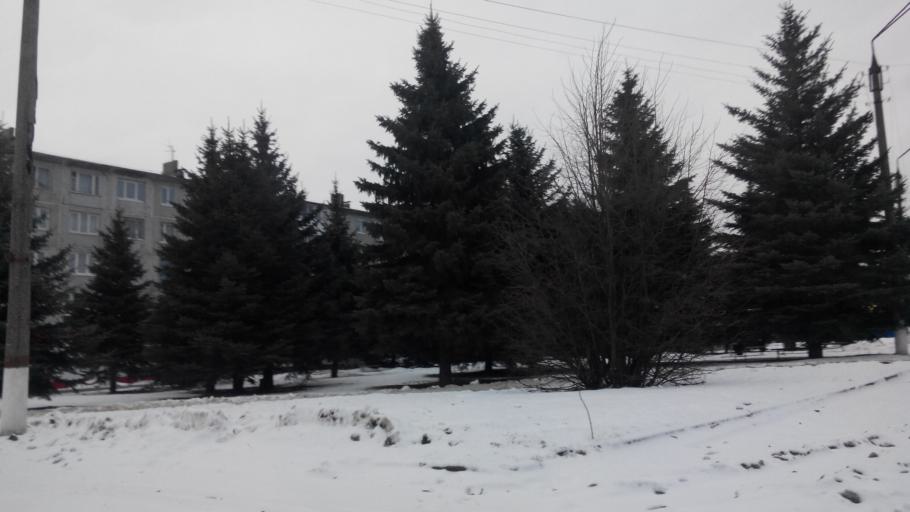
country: RU
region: Tula
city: Podlesnyy
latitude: 53.9651
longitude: 38.2889
